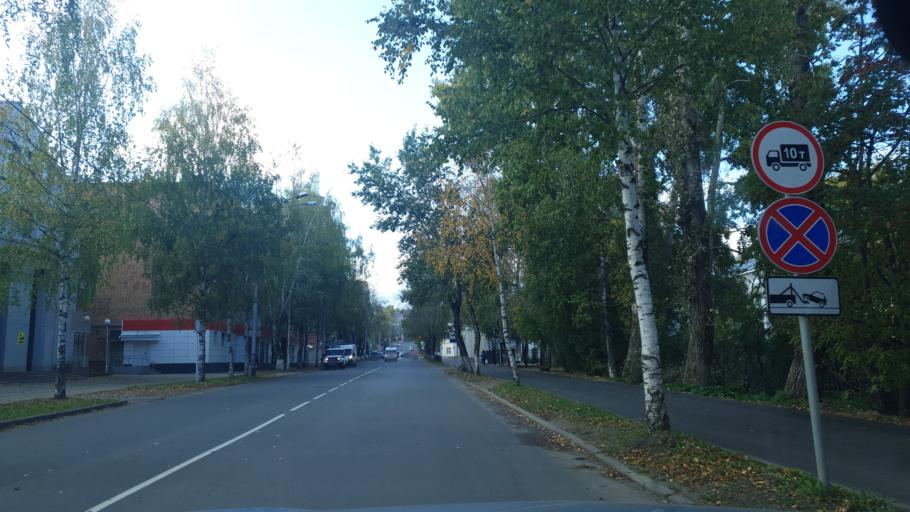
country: RU
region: Komi Republic
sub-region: Syktyvdinskiy Rayon
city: Syktyvkar
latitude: 61.6658
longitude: 50.8472
